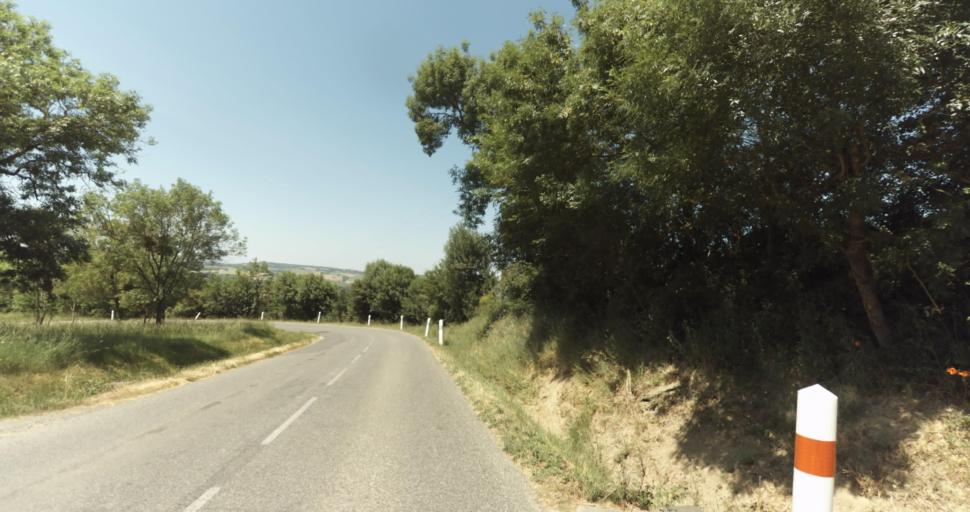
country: FR
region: Midi-Pyrenees
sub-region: Departement de la Haute-Garonne
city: Levignac
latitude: 43.6356
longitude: 1.1782
